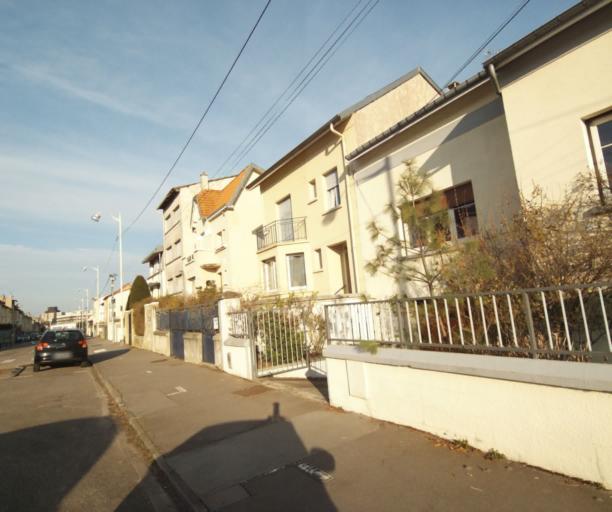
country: FR
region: Lorraine
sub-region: Departement de Meurthe-et-Moselle
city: Laxou
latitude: 48.6945
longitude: 6.1438
